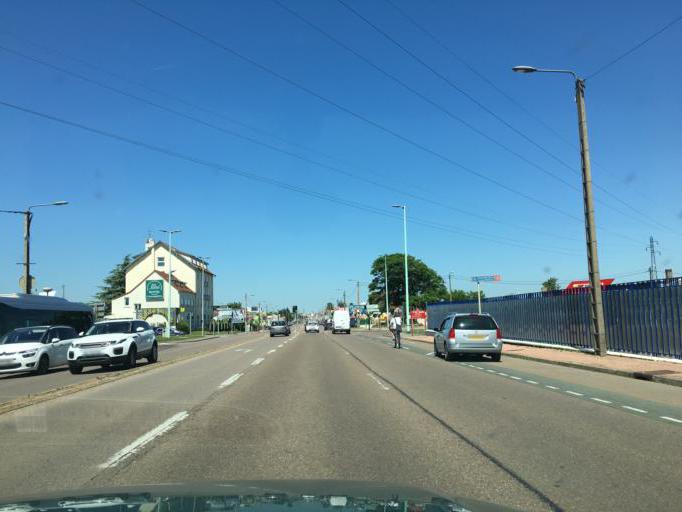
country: FR
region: Bourgogne
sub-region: Departement de la Cote-d'Or
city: Chenove
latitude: 47.2871
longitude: 5.0122
